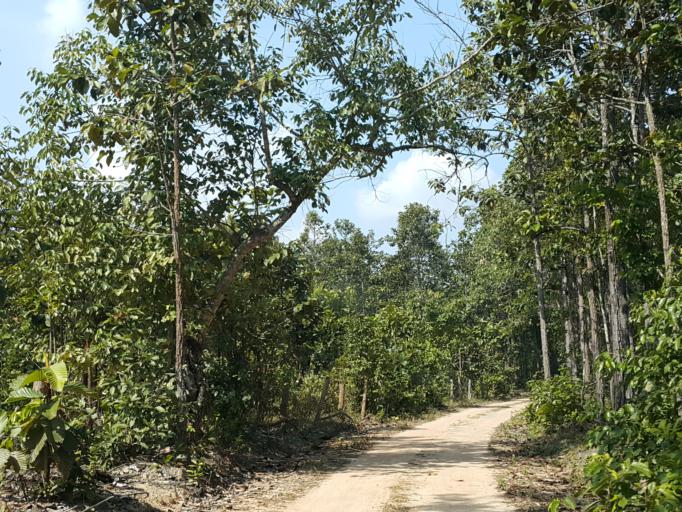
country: TH
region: Chiang Mai
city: Hot
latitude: 18.1249
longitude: 98.4382
